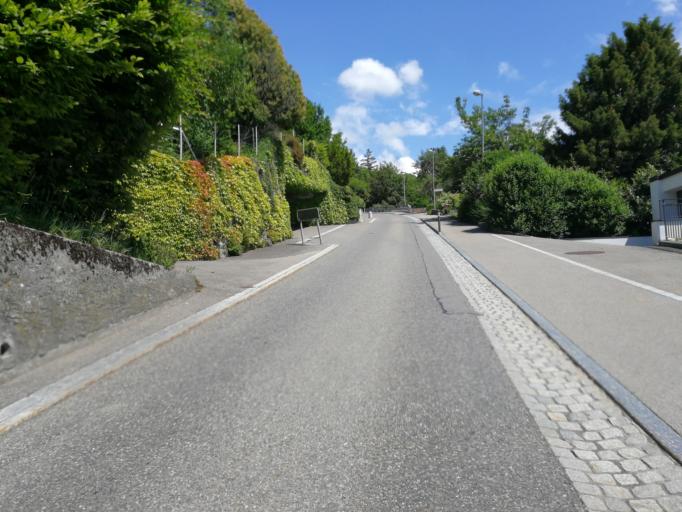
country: CH
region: Zurich
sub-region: Bezirk Meilen
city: Uetikon / Grossdorf
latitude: 47.2707
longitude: 8.6849
